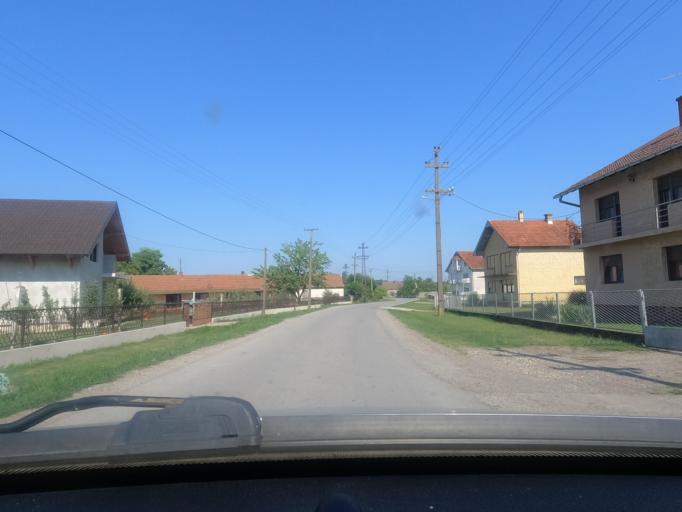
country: RS
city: Bogosavac
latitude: 44.7528
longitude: 19.5739
